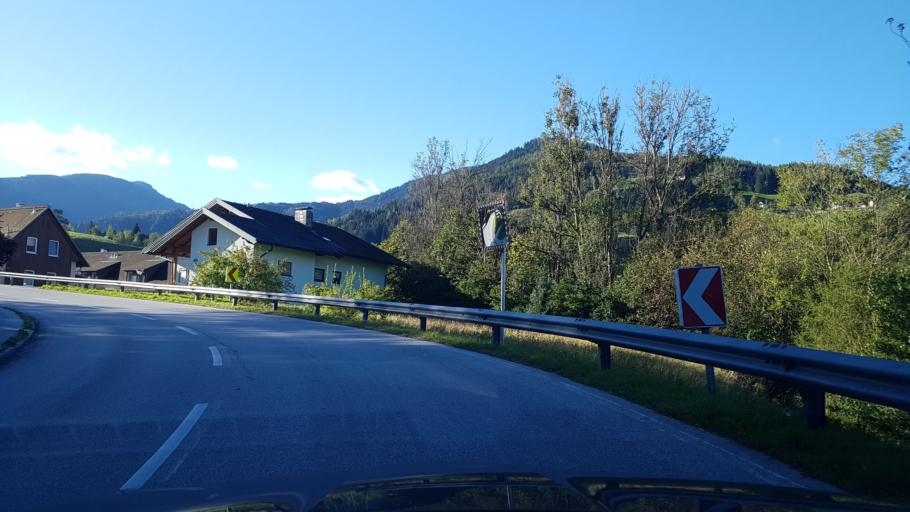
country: AT
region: Styria
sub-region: Politischer Bezirk Liezen
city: Grosssolk
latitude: 47.4347
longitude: 13.9425
